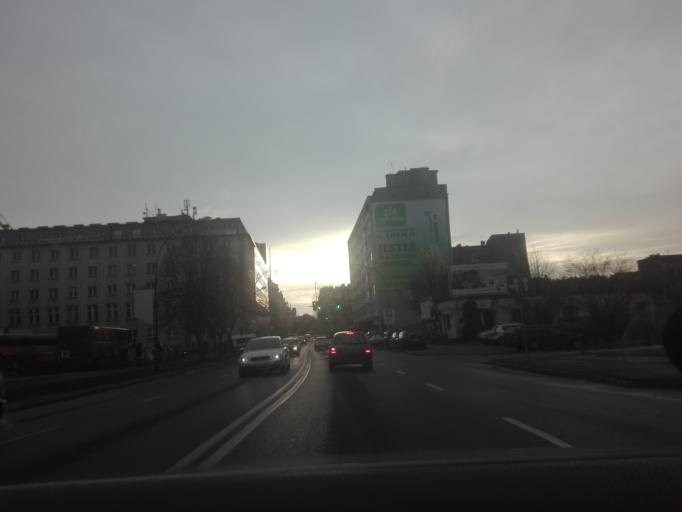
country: PL
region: Silesian Voivodeship
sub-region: Katowice
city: Katowice
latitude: 50.2634
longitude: 19.0171
